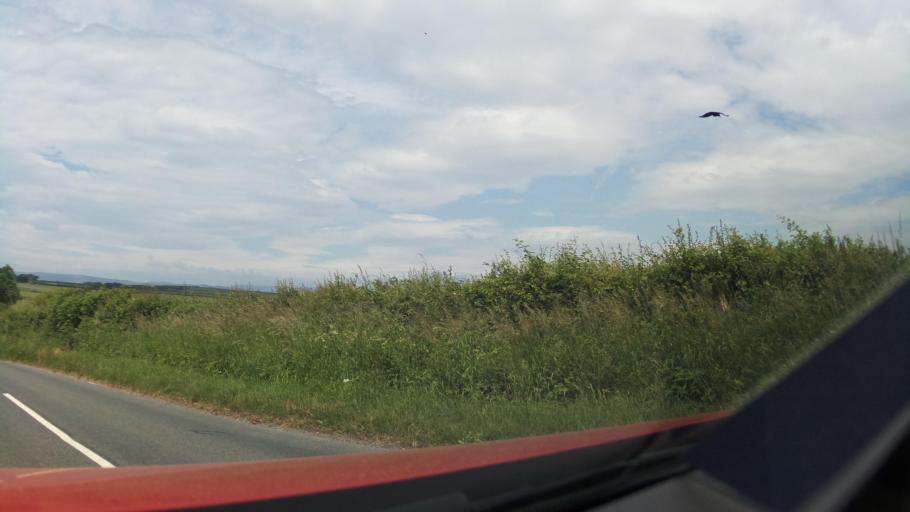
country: GB
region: Wales
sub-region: Vale of Glamorgan
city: Wick
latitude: 51.4476
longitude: -3.5742
